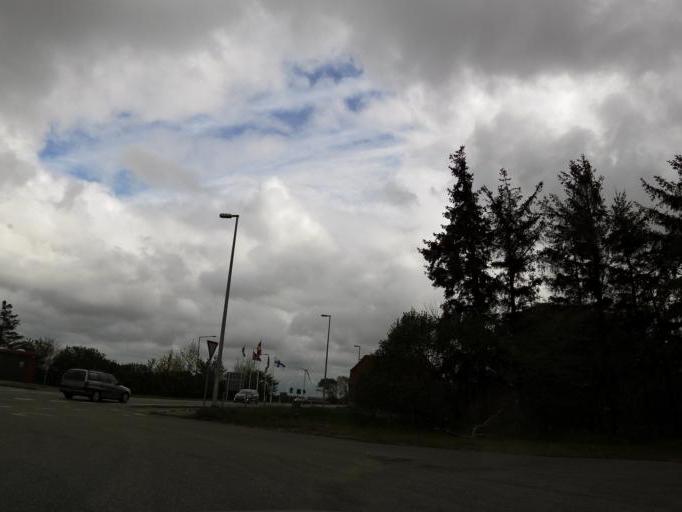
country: DE
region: Schleswig-Holstein
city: Suderlugum
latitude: 54.9049
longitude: 8.9095
